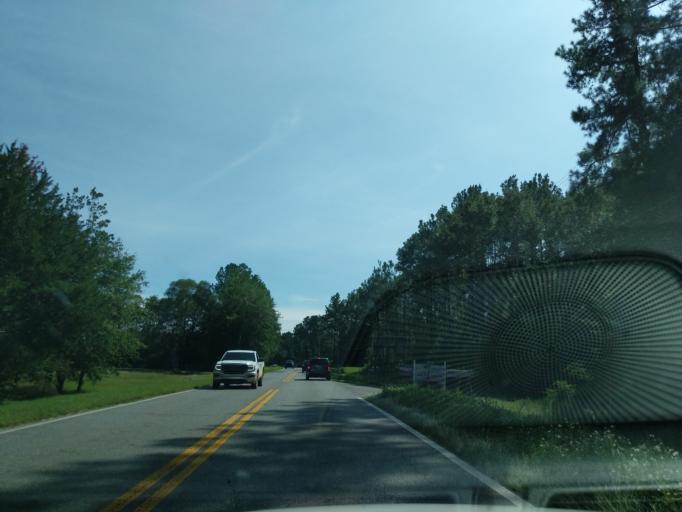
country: US
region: Florida
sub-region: Okaloosa County
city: Crestview
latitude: 30.7357
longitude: -86.6232
